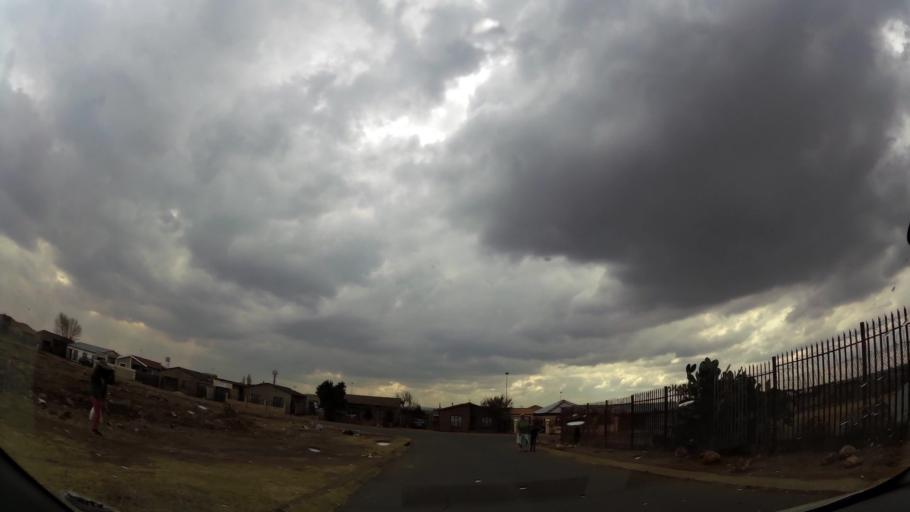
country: ZA
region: Gauteng
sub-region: Ekurhuleni Metropolitan Municipality
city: Germiston
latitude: -26.3656
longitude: 28.1604
